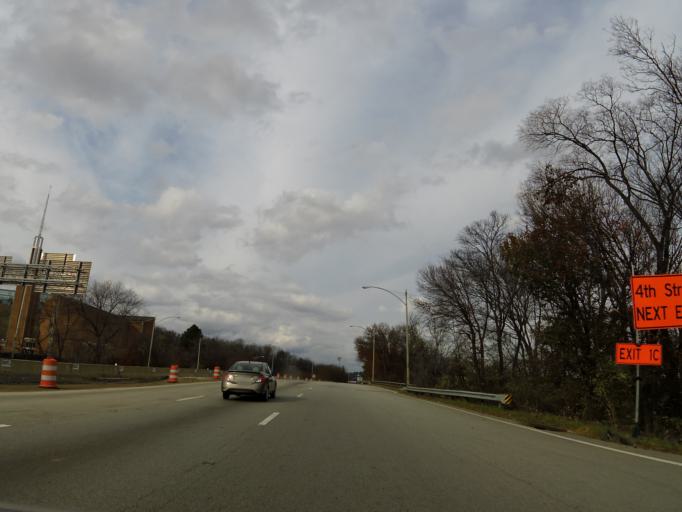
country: US
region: Tennessee
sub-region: Hamilton County
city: Chattanooga
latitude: 35.0489
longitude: -85.3141
